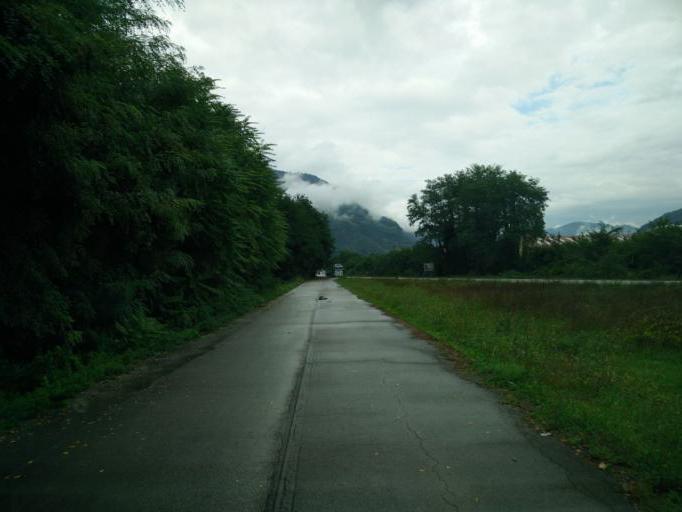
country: IT
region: Tuscany
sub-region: Provincia di Lucca
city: Valdottavo
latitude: 43.9504
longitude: 10.4991
